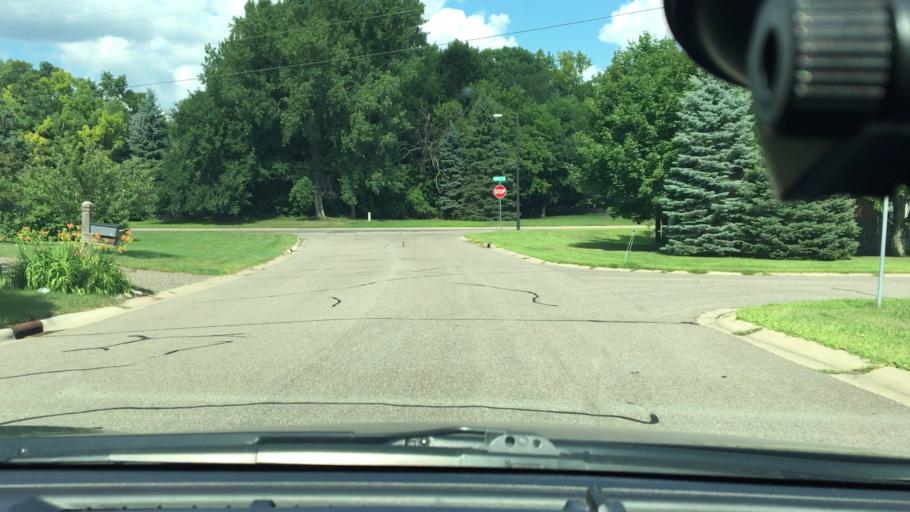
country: US
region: Minnesota
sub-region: Hennepin County
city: Plymouth
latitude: 45.0341
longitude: -93.4365
